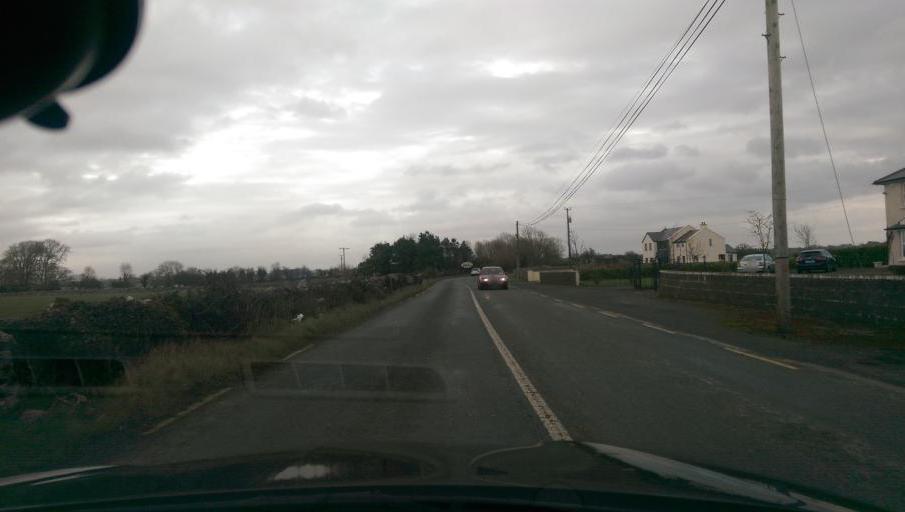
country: IE
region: Connaught
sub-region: County Galway
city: Oranmore
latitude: 53.3202
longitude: -8.8585
